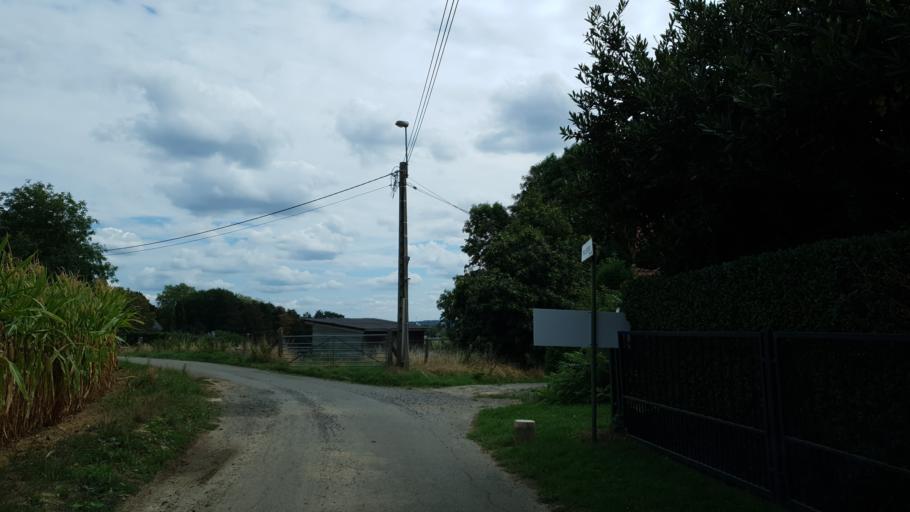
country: BE
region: Flanders
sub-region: Provincie Vlaams-Brabant
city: Herent
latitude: 50.8922
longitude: 4.6743
